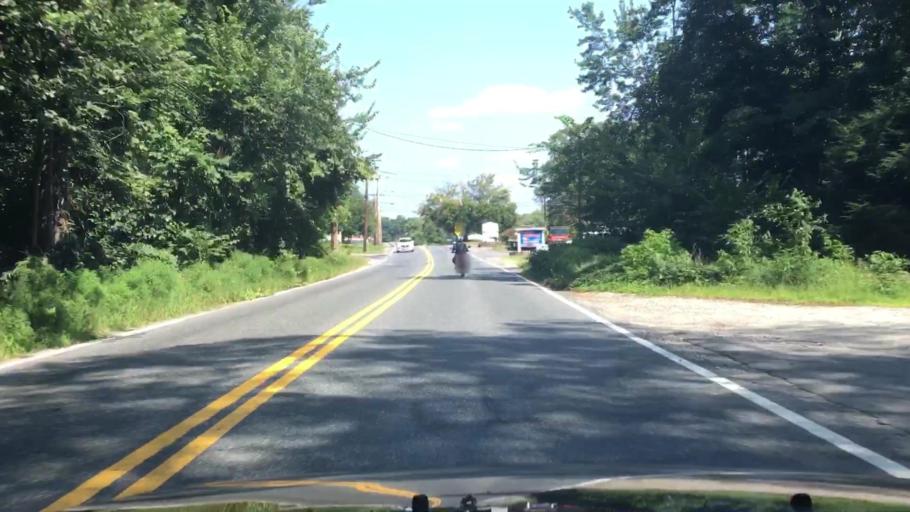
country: US
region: Massachusetts
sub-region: Middlesex County
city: Holliston
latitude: 42.1790
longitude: -71.4553
